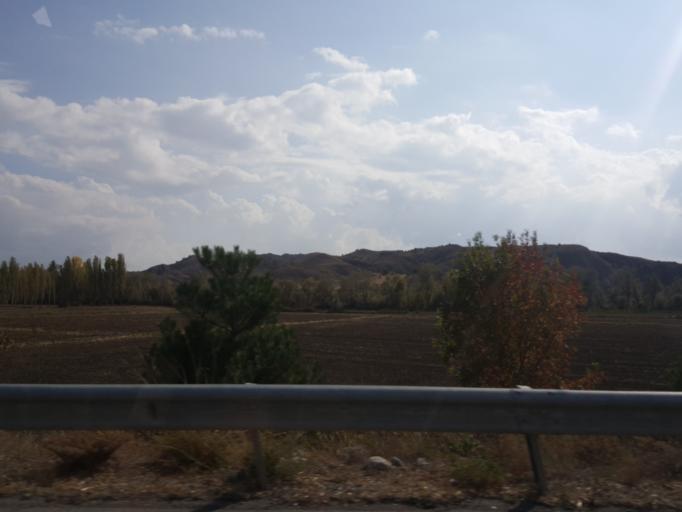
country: TR
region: Corum
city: Sungurlu
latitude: 40.1824
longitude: 34.4842
